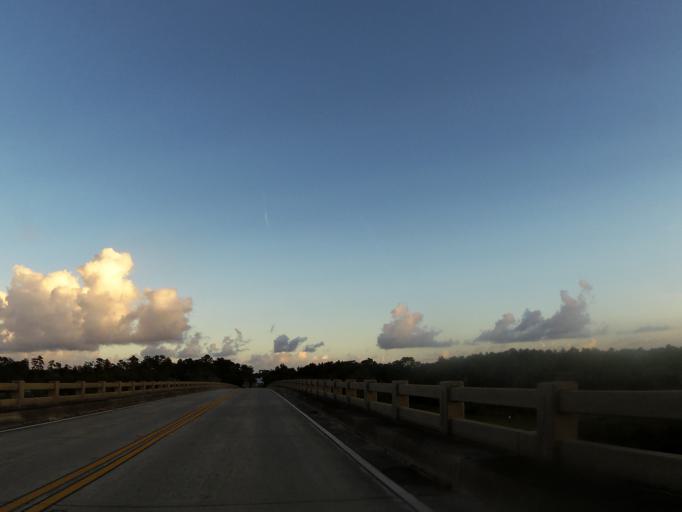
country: US
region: Georgia
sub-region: Camden County
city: Woodbine
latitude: 30.9751
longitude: -81.7257
